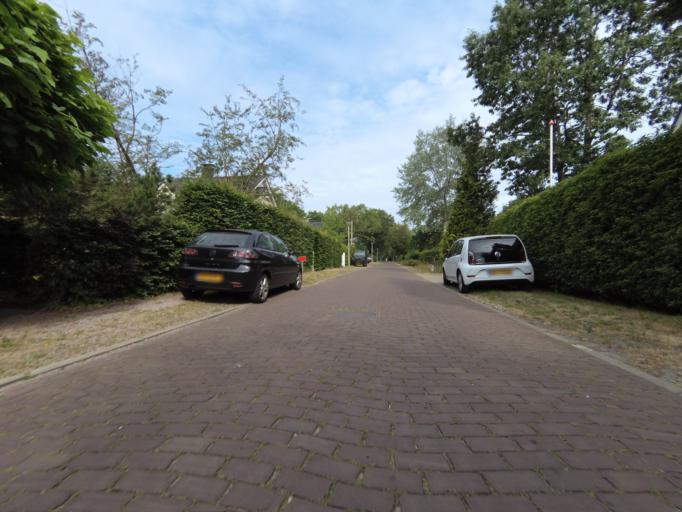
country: NL
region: Overijssel
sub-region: Gemeente Hengelo
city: Hengelo
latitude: 52.2090
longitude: 6.7939
